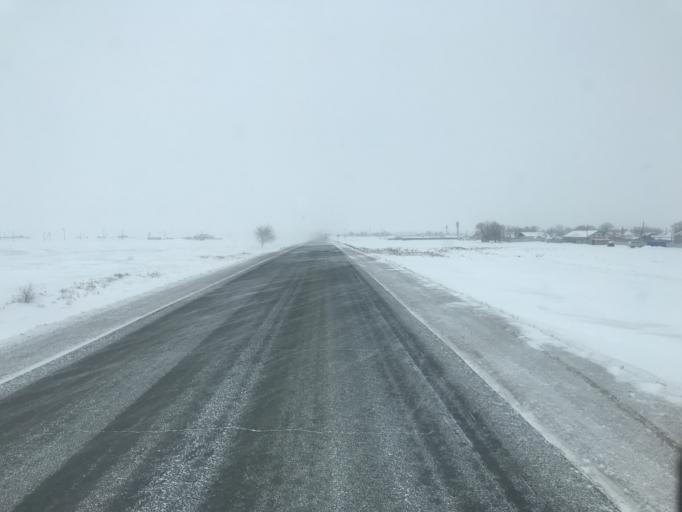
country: KZ
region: Batys Qazaqstan
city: Chapaev
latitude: 50.5042
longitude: 51.0536
